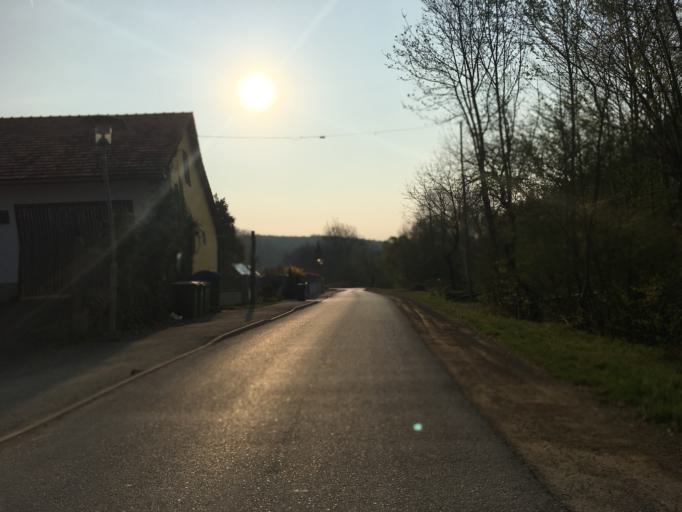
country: AT
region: Styria
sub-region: Politischer Bezirk Graz-Umgebung
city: Nestelbach bei Graz
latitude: 47.0836
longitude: 15.6208
